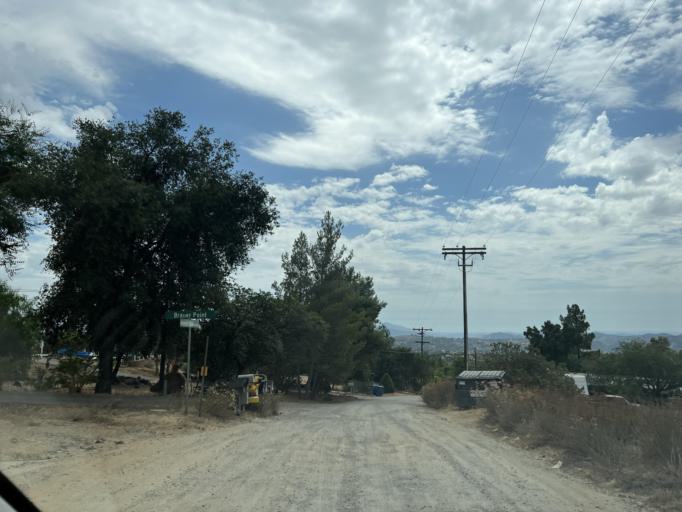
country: US
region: California
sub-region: San Diego County
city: Alpine
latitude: 32.8524
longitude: -116.7428
